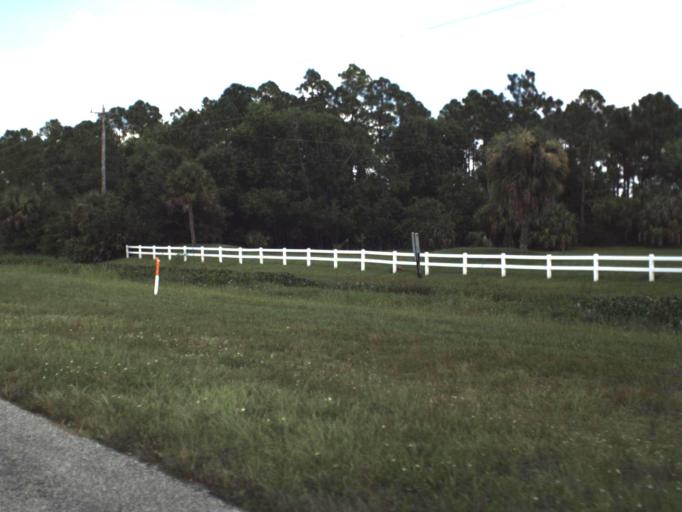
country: US
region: Florida
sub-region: Lee County
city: Suncoast Estates
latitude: 26.7720
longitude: -81.9323
